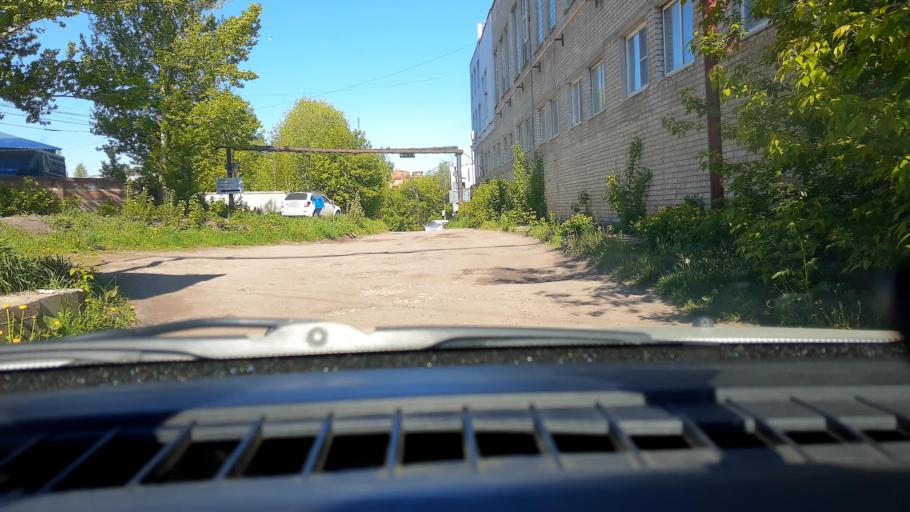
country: RU
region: Nizjnij Novgorod
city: Bor
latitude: 56.3112
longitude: 44.0568
